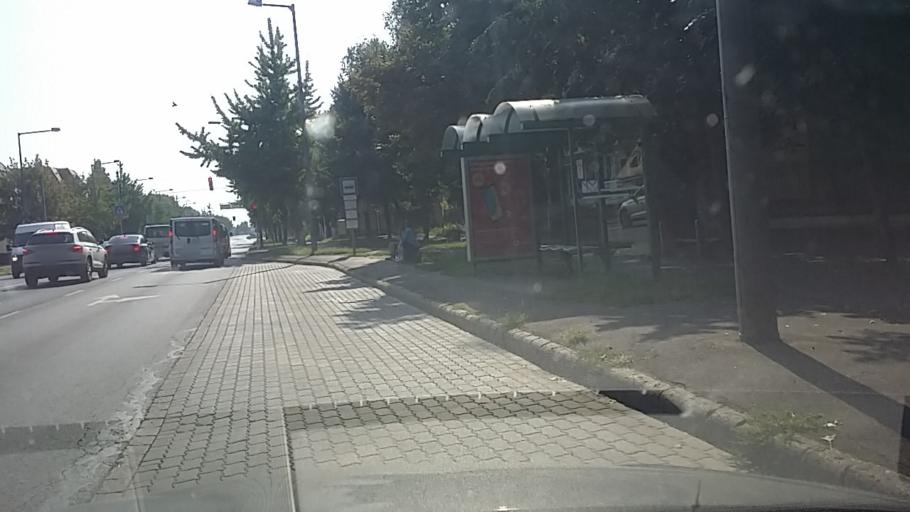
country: HU
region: Bekes
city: Bekescsaba
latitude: 46.6820
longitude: 21.1034
